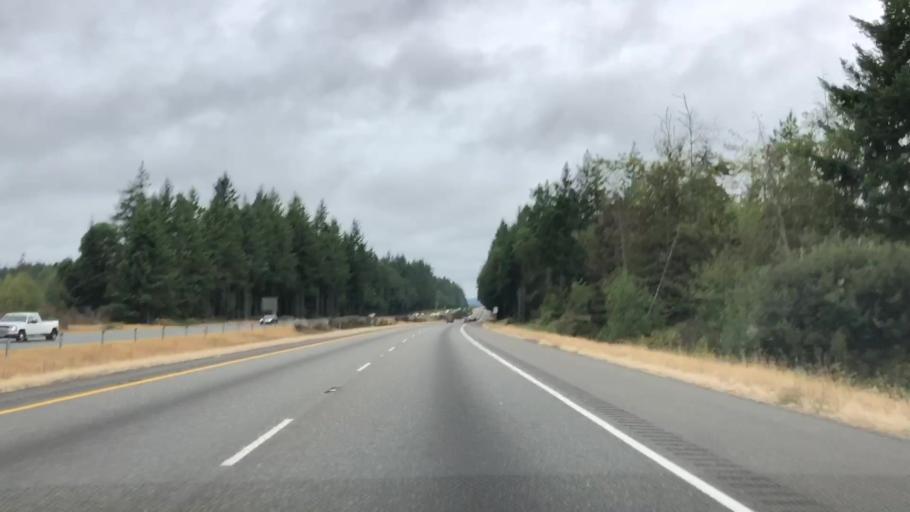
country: US
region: Washington
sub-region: Pierce County
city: Gig Harbor
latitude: 47.3383
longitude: -122.6051
